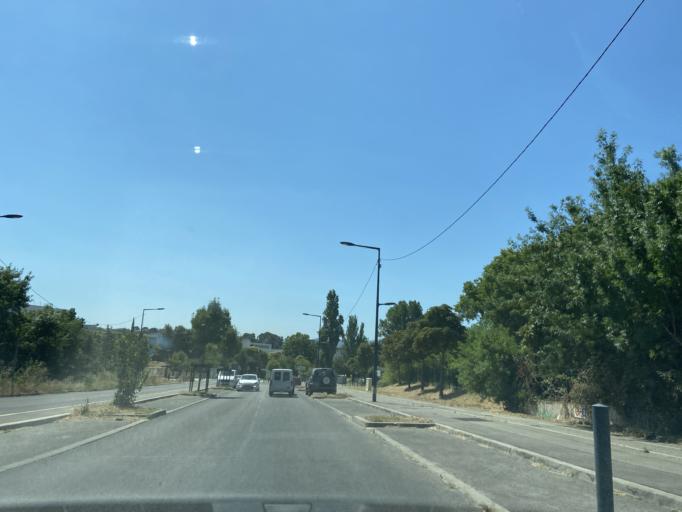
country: FR
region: Provence-Alpes-Cote d'Azur
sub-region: Departement des Bouches-du-Rhone
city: Plan-de-Cuques
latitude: 43.3433
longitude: 5.4357
